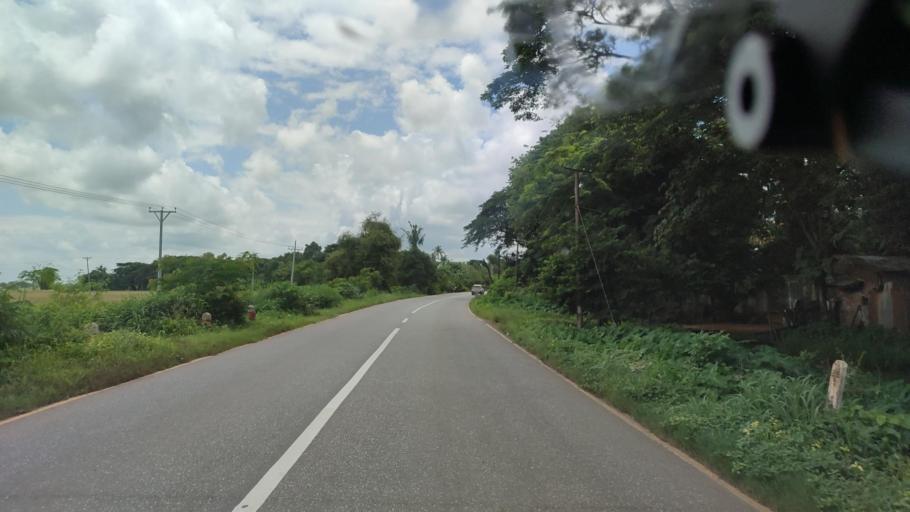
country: MM
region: Bago
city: Letpandan
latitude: 18.1579
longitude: 95.6839
